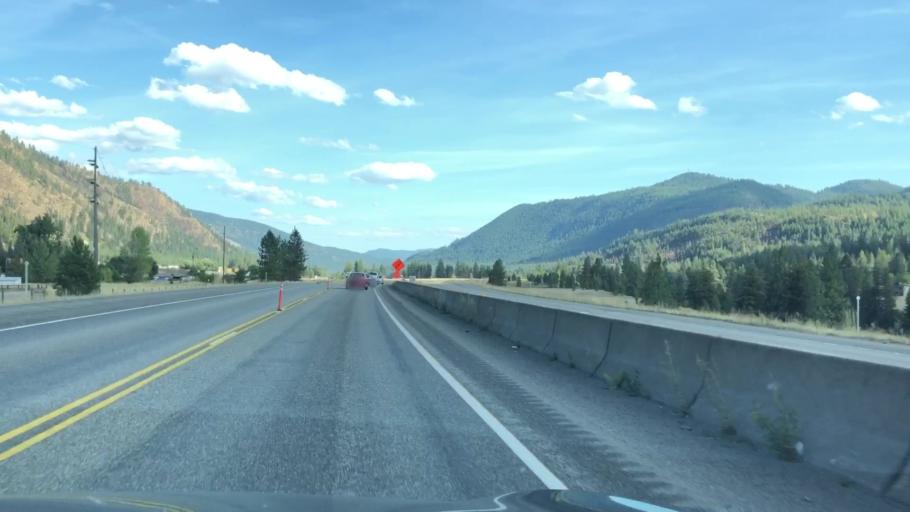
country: US
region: Montana
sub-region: Mineral County
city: Superior
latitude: 47.2146
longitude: -114.9441
